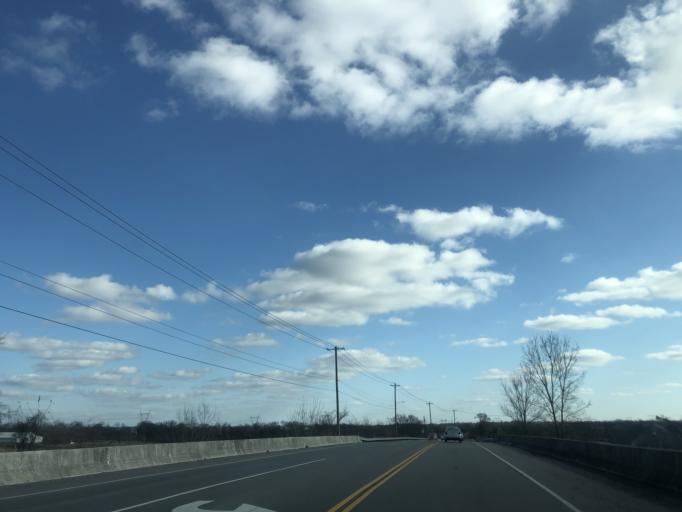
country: US
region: Tennessee
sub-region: Sumner County
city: Shackle Island
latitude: 36.3565
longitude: -86.5315
